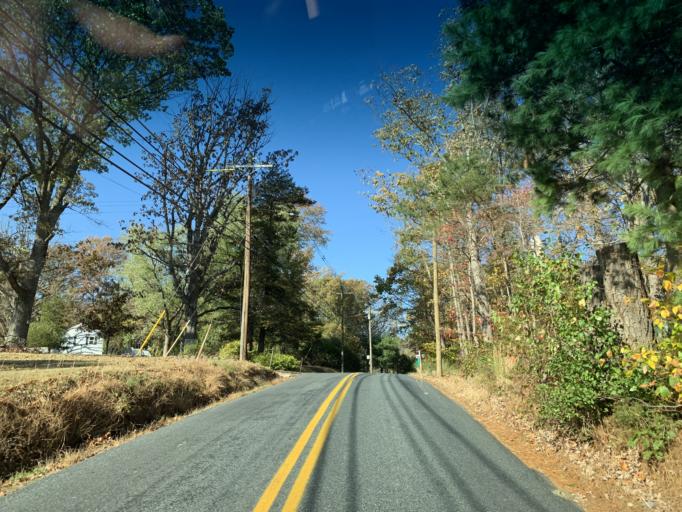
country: US
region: Maryland
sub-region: Harford County
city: Joppatowne
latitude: 39.4533
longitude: -76.3387
